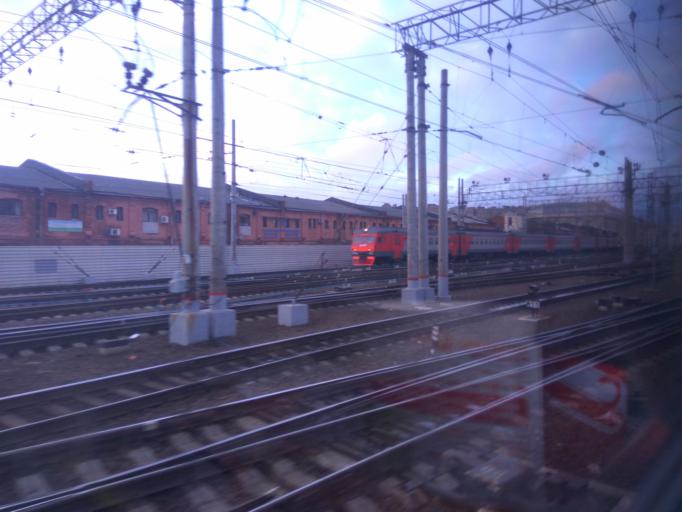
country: RU
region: St.-Petersburg
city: Centralniy
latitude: 59.9231
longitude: 30.3646
